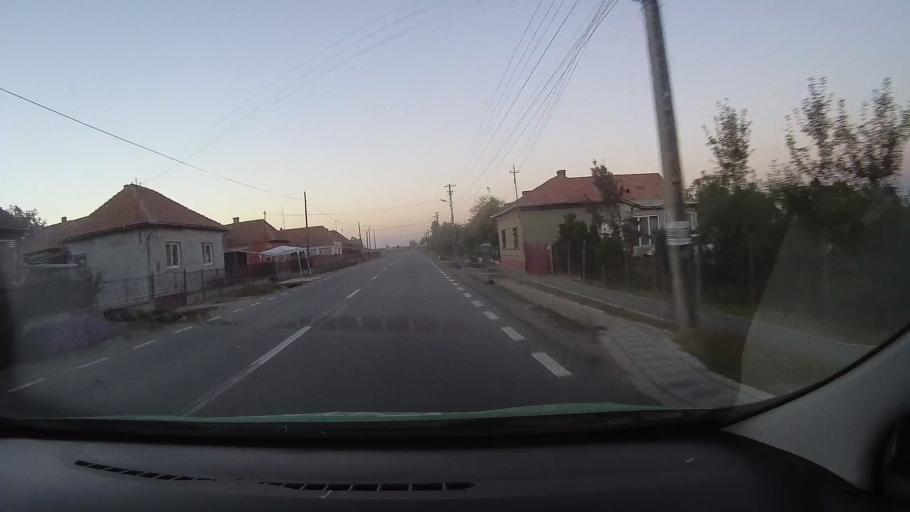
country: RO
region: Bihor
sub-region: Comuna Tarcea
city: Tarcea
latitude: 47.4651
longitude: 22.1665
